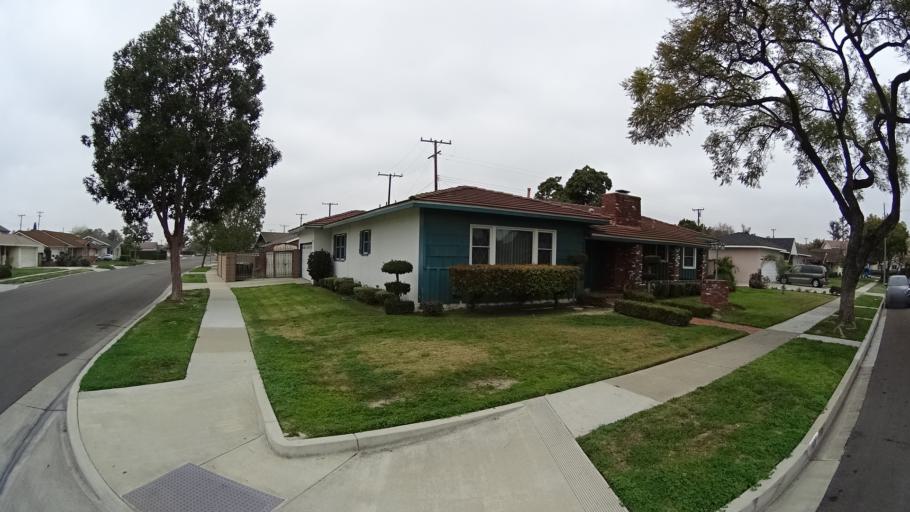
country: US
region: California
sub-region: Orange County
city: Stanton
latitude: 33.8197
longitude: -118.0031
